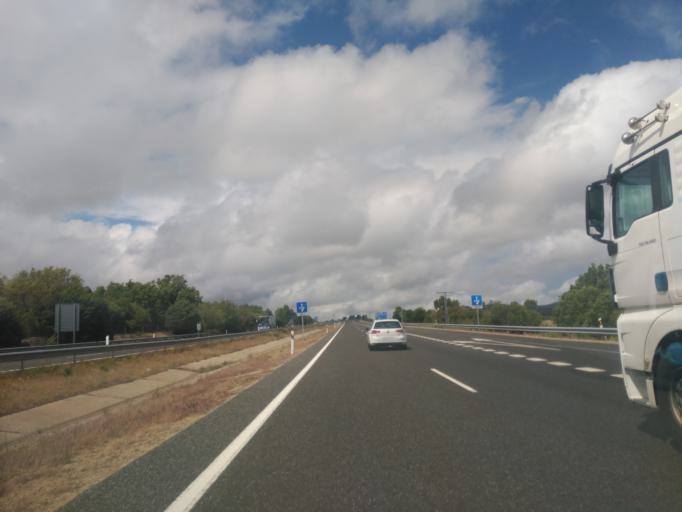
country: ES
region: Castille and Leon
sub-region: Provincia de Salamanca
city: Sorihuela
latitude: 40.4550
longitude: -5.6808
